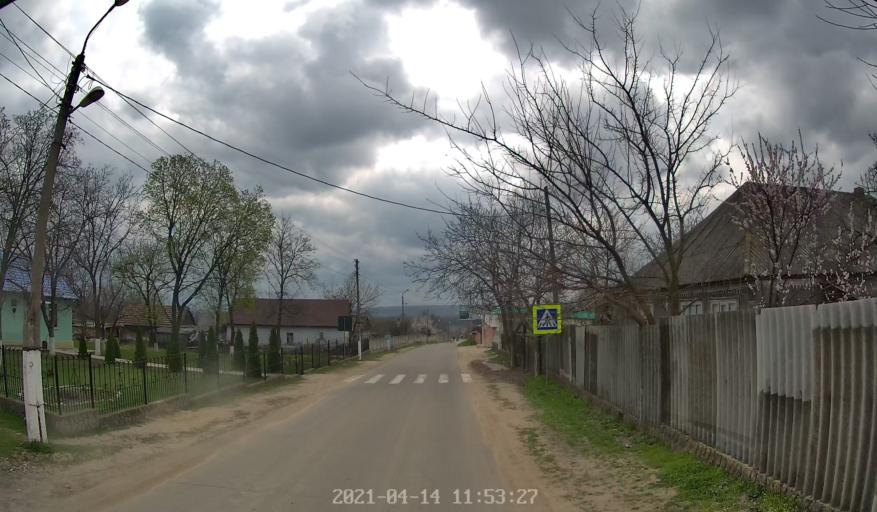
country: MD
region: Criuleni
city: Criuleni
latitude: 47.1685
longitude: 29.1967
